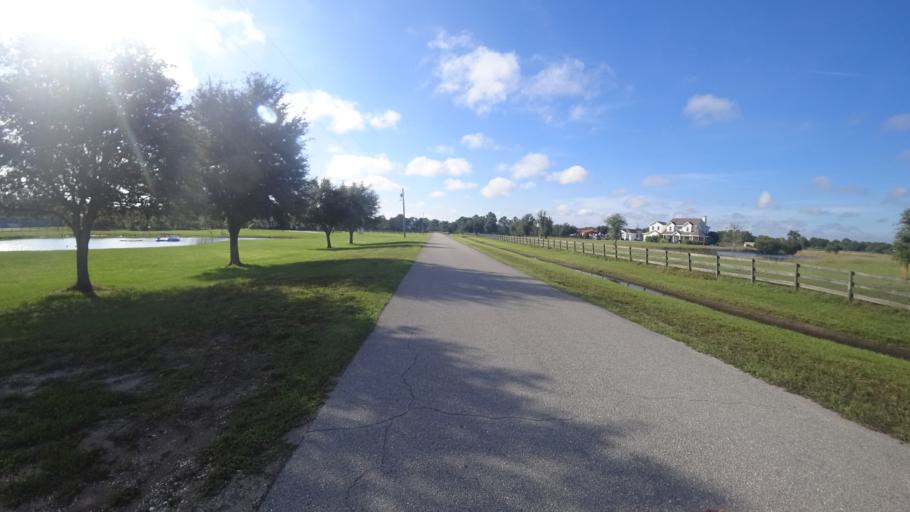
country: US
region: Florida
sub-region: Sarasota County
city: The Meadows
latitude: 27.4202
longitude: -82.3244
